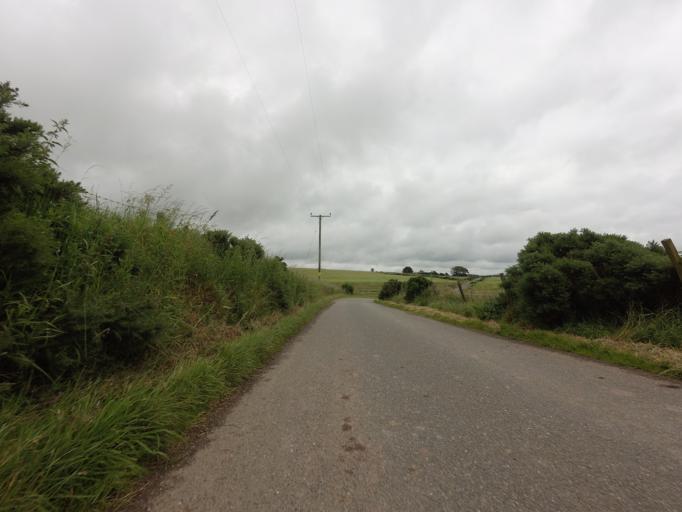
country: GB
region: Scotland
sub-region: Aberdeenshire
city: Turriff
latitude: 57.5448
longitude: -2.2805
